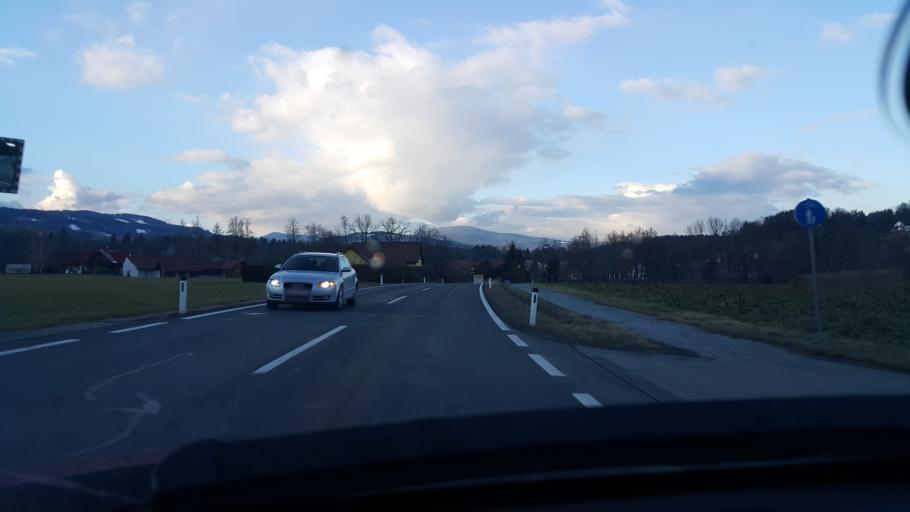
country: AT
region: Styria
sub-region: Politischer Bezirk Deutschlandsberg
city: Hollenegg
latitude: 46.7814
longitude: 15.2427
